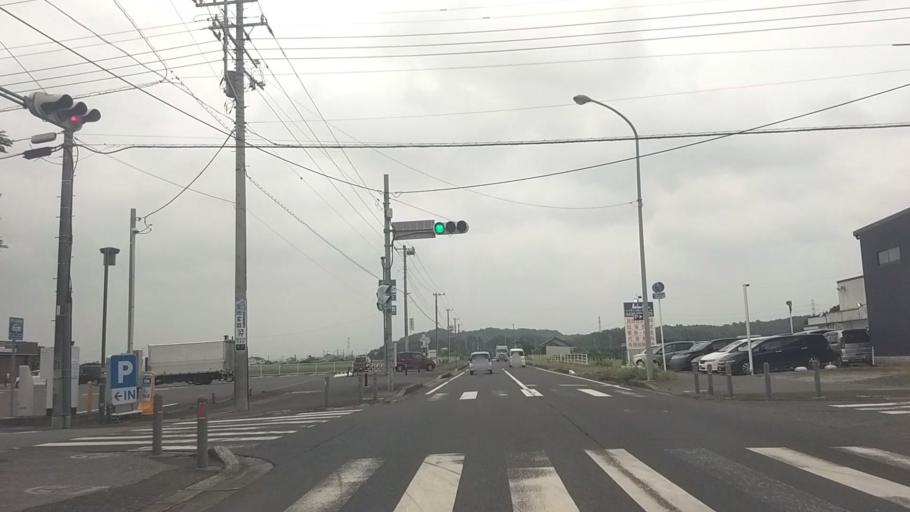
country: JP
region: Chiba
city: Kisarazu
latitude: 35.3883
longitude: 139.9832
